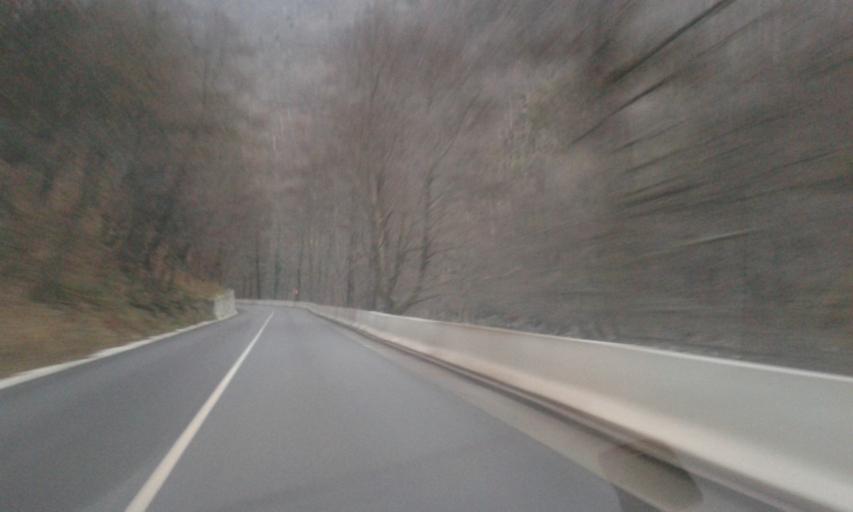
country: RO
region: Gorj
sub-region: Comuna Bumbesti-Jiu
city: Bumbesti-Jiu
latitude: 45.2521
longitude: 23.3854
